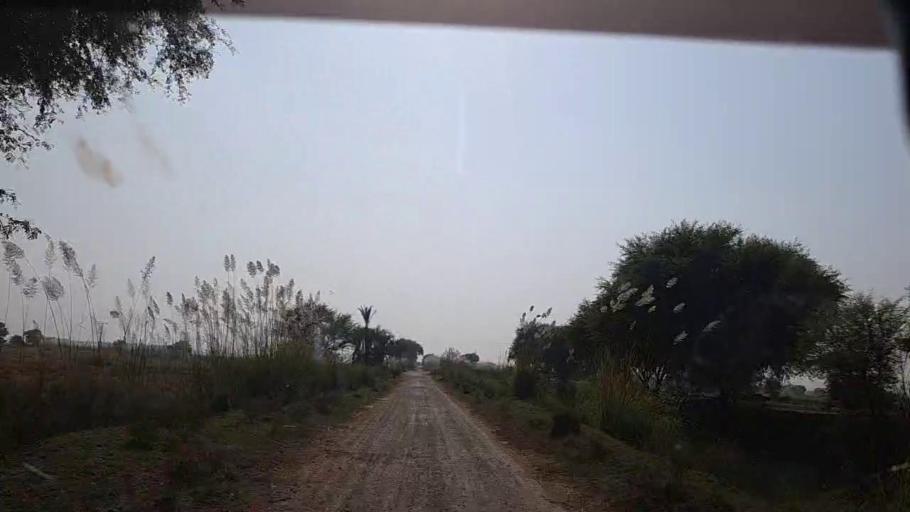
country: PK
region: Sindh
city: Shikarpur
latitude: 28.1161
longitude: 68.6588
